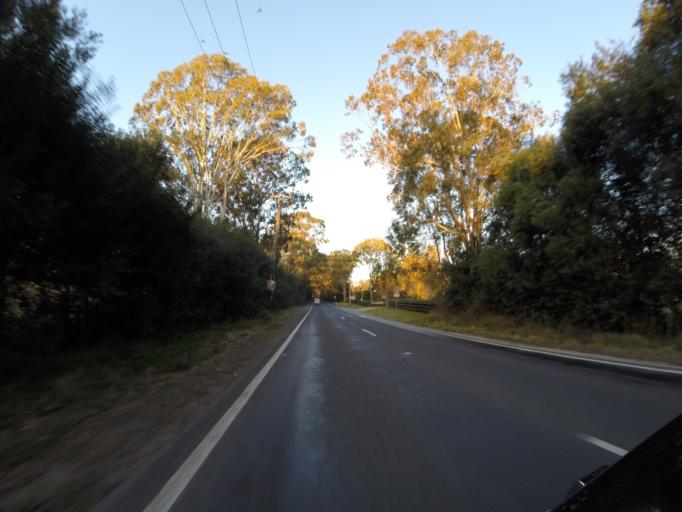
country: AU
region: New South Wales
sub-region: Camden
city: Cobbitty
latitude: -34.0159
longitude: 150.6958
